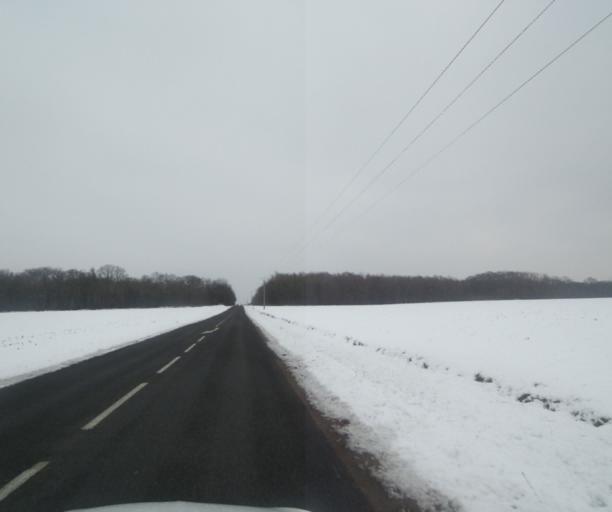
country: FR
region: Champagne-Ardenne
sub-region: Departement de la Haute-Marne
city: Villiers-en-Lieu
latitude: 48.6072
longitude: 4.8824
